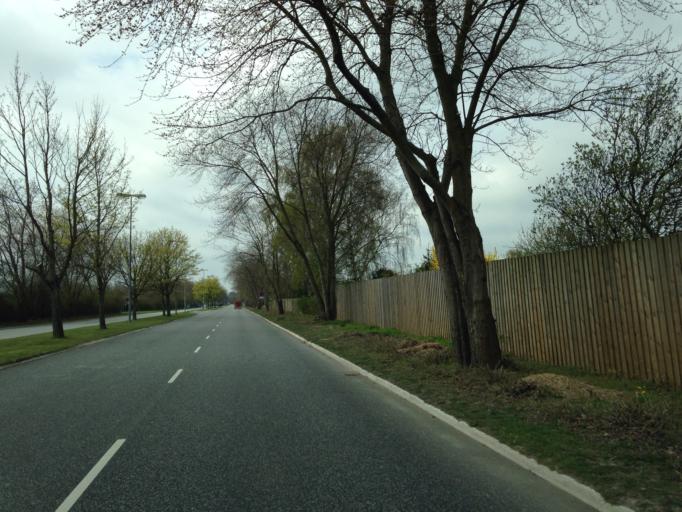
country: DK
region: Capital Region
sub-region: Ishoj Kommune
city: Ishoj
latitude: 55.6136
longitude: 12.3388
